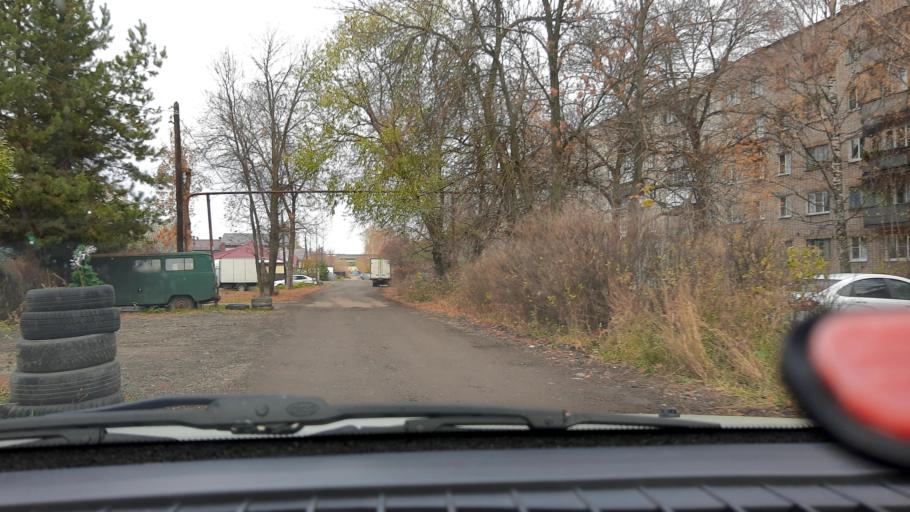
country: RU
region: Nizjnij Novgorod
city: Nizhniy Novgorod
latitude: 56.3076
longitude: 43.9198
